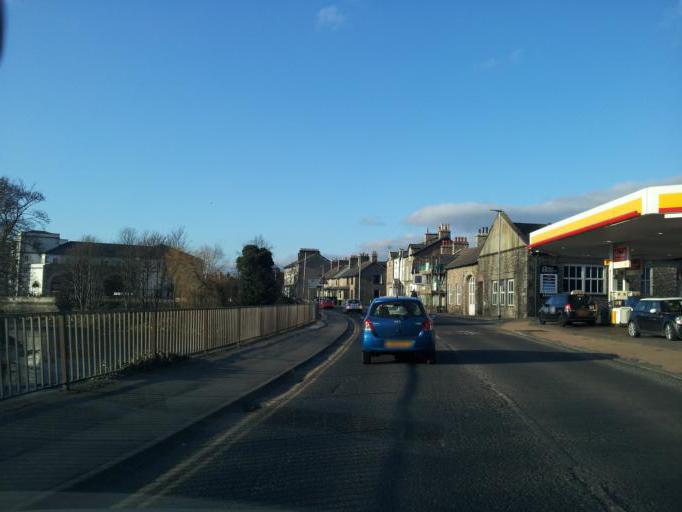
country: GB
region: England
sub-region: Cumbria
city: Kendal
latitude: 54.3177
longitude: -2.7416
